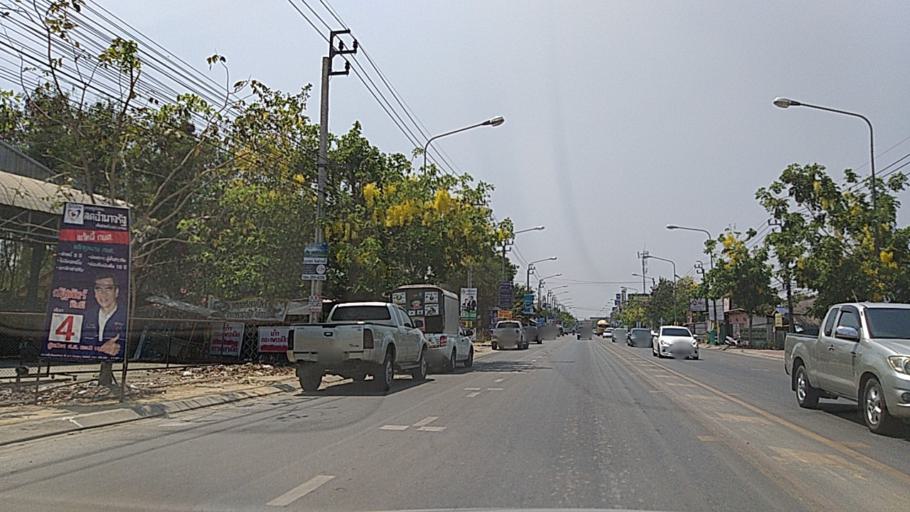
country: TH
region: Nonthaburi
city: Bang Bua Thong
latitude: 13.9084
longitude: 100.3942
